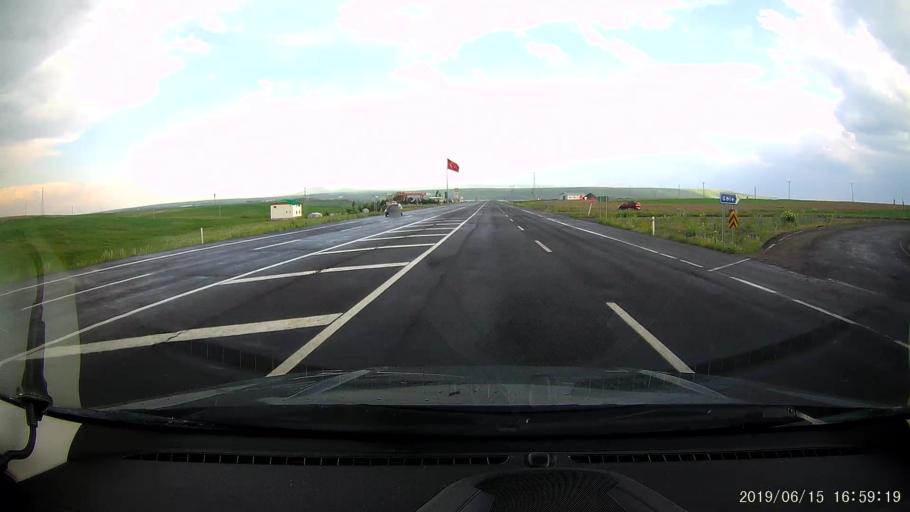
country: TR
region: Kars
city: Susuz
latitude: 40.7535
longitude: 43.1498
